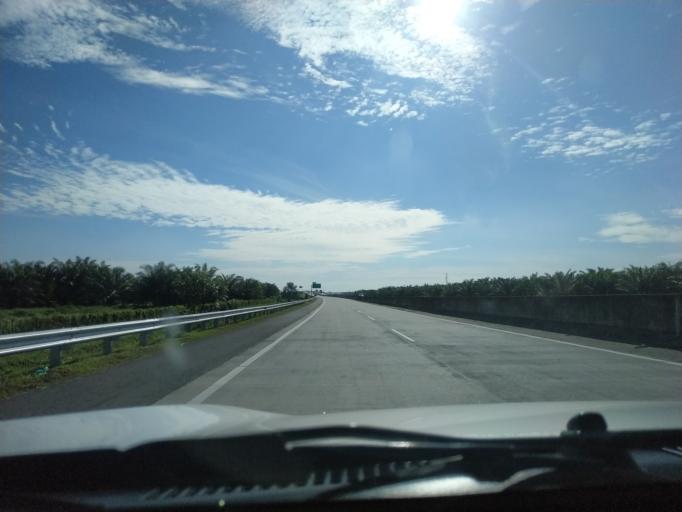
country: ID
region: North Sumatra
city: Perbaungan
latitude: 3.5316
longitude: 98.8793
